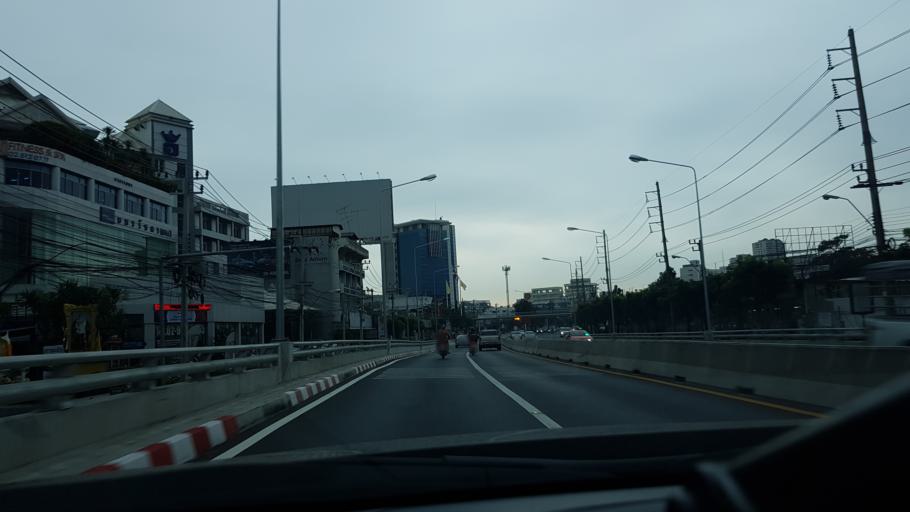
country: TH
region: Bangkok
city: Chatuchak
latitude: 13.8253
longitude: 100.5717
